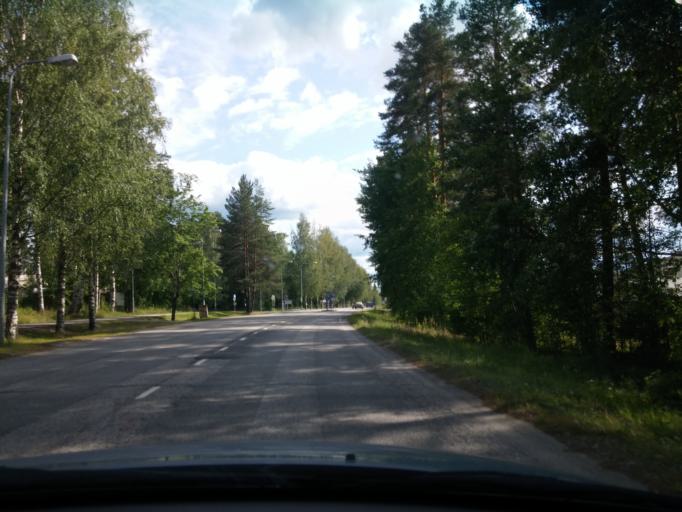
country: FI
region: Central Finland
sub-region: Keuruu
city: Keuruu
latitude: 62.2646
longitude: 24.6991
